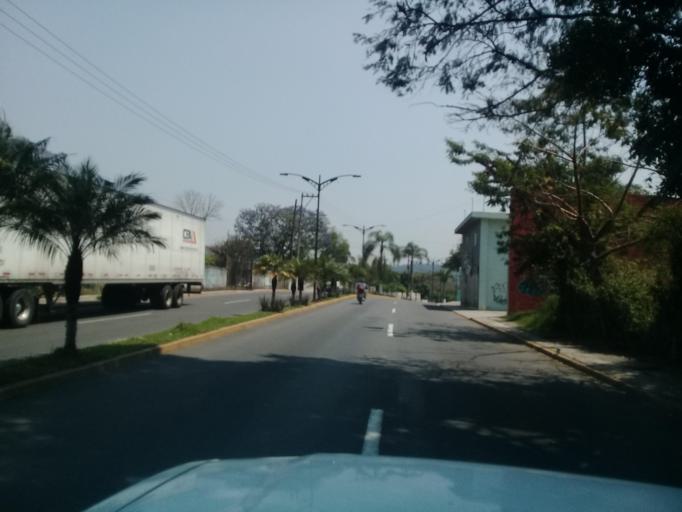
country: MX
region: Veracruz
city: Ixtac Zoquitlan
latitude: 18.8625
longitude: -97.0510
